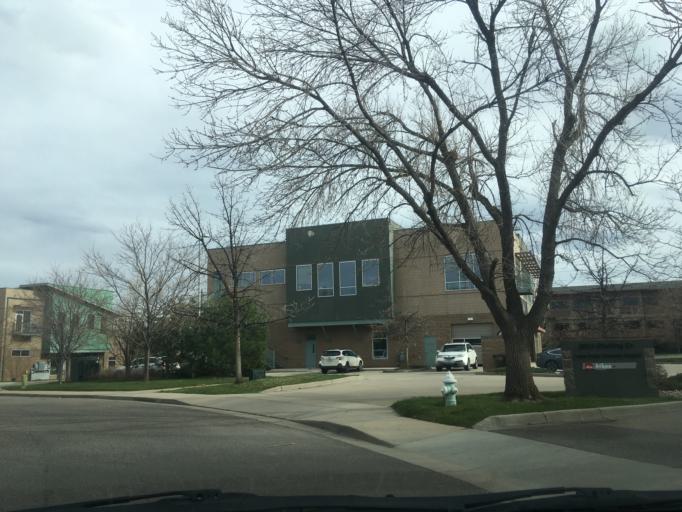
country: US
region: Colorado
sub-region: Boulder County
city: Boulder
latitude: 40.0301
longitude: -105.2282
